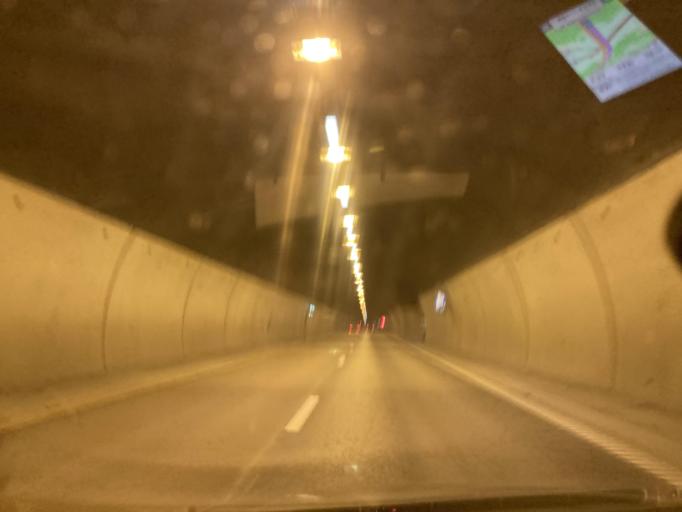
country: NO
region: Akershus
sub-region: Eidsvoll
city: Eidsvoll
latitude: 60.3385
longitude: 11.1993
